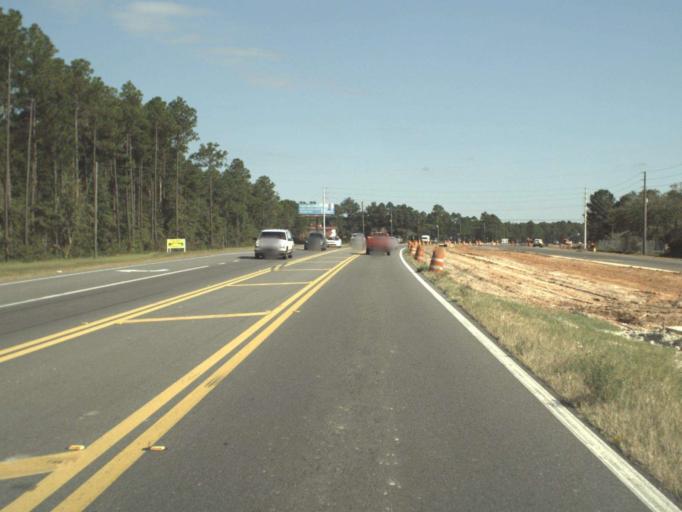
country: US
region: Florida
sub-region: Walton County
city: Freeport
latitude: 30.4332
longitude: -86.1532
